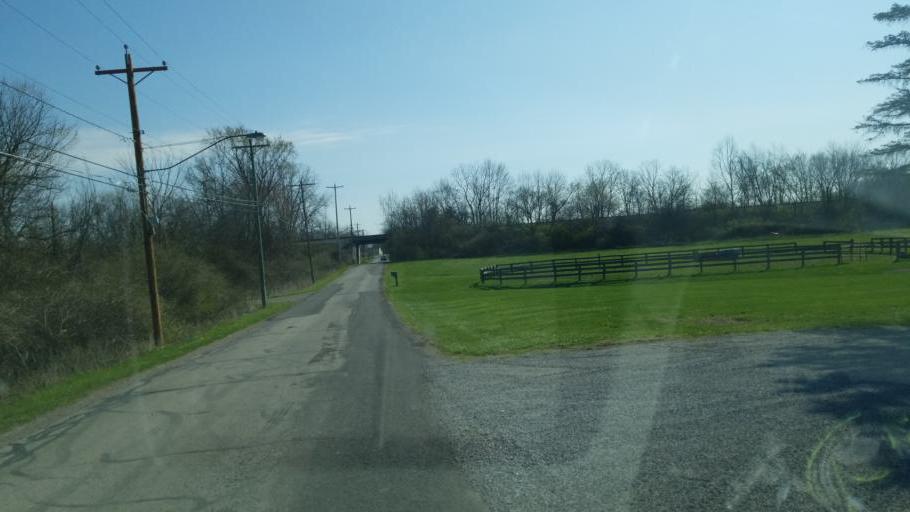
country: US
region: Ohio
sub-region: Delaware County
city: Delaware
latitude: 40.3046
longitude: -83.0495
